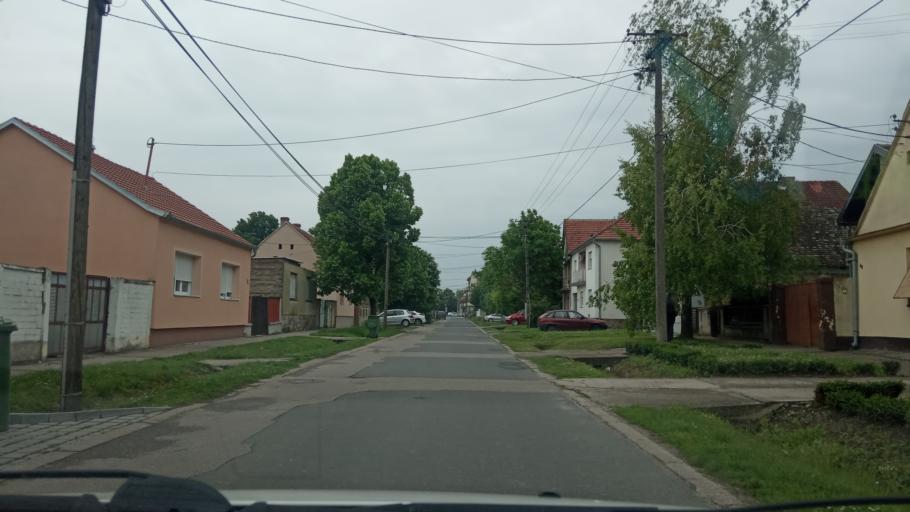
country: RS
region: Autonomna Pokrajina Vojvodina
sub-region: Sremski Okrug
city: Stara Pazova
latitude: 44.9882
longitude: 20.1542
